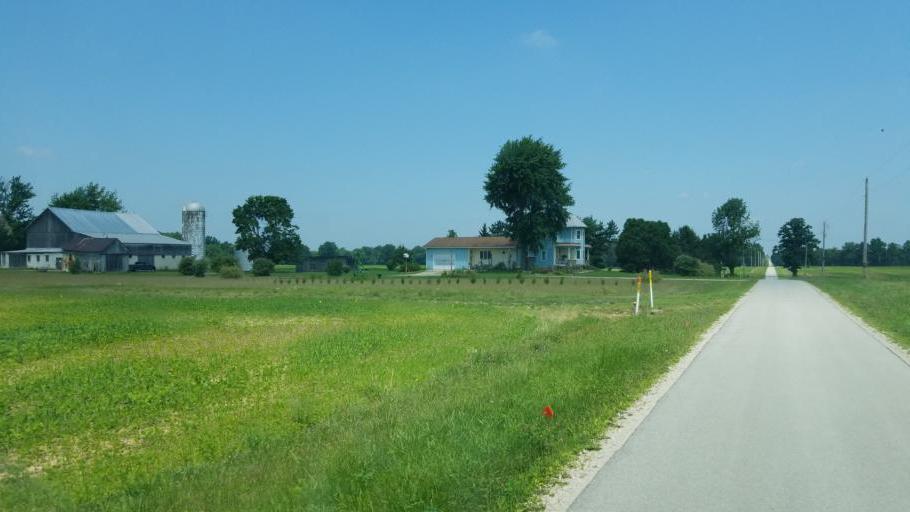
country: US
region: Ohio
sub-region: Sandusky County
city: Green Springs
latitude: 41.0685
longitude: -82.9769
